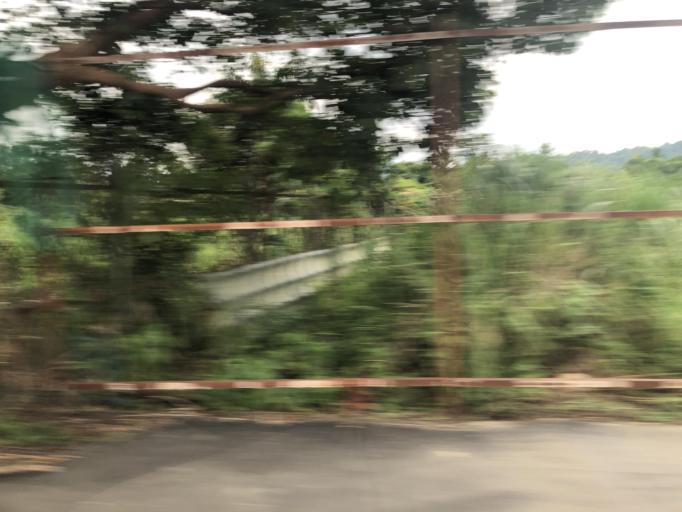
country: TW
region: Taiwan
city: Daxi
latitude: 24.9167
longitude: 121.3621
